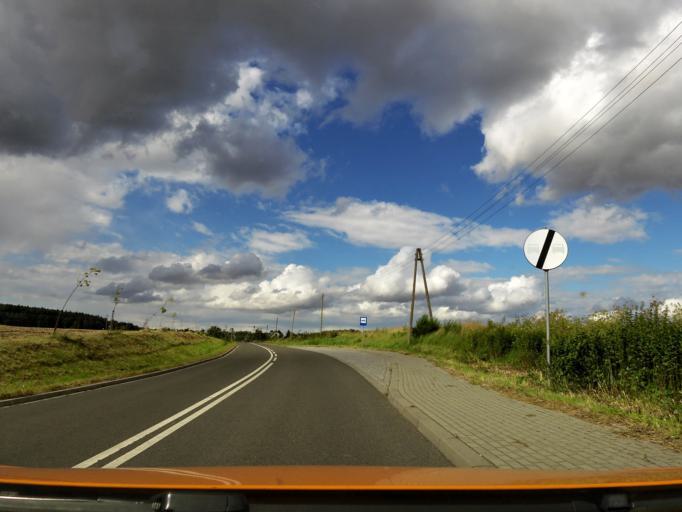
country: PL
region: West Pomeranian Voivodeship
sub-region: Powiat kolobrzeski
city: Ryman
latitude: 53.9726
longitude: 15.4904
